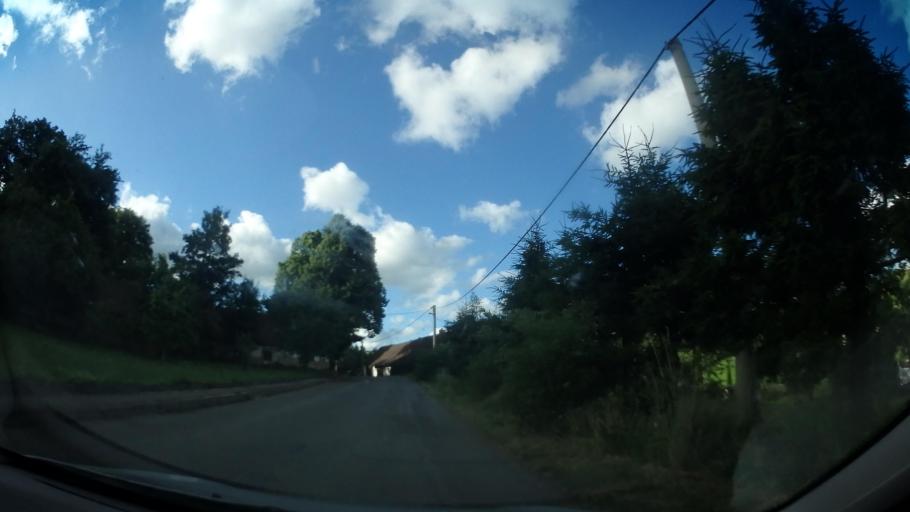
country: CZ
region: Vysocina
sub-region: Okres Zd'ar nad Sazavou
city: Jimramov
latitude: 49.5759
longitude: 16.1889
